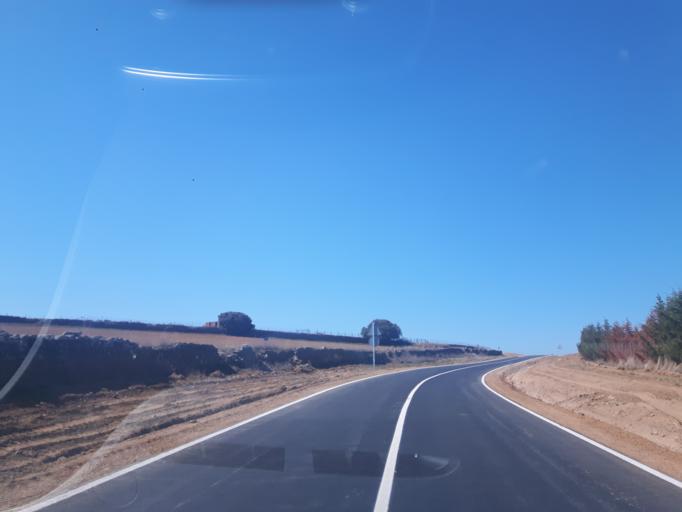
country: ES
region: Castille and Leon
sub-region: Provincia de Salamanca
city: Alba de Tormes
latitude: 40.8233
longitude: -5.5294
